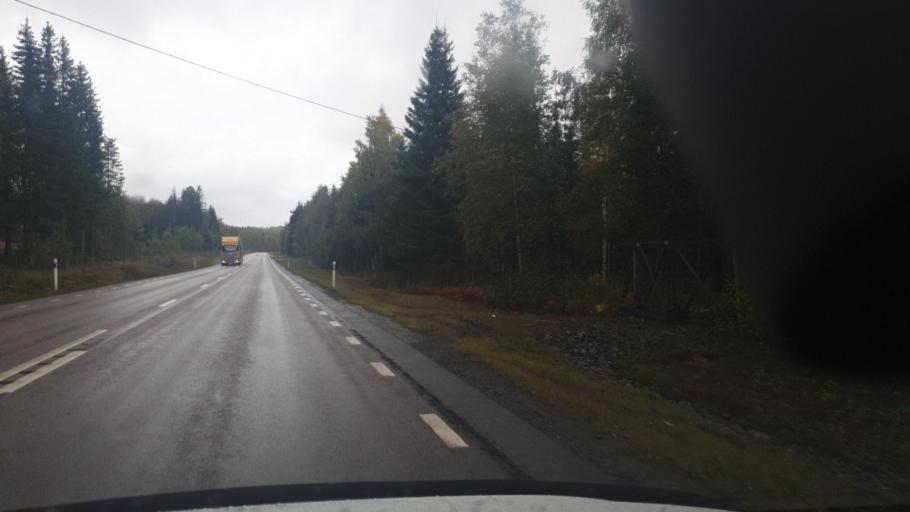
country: SE
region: Vaermland
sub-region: Sunne Kommun
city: Sunne
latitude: 59.7661
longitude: 13.1072
